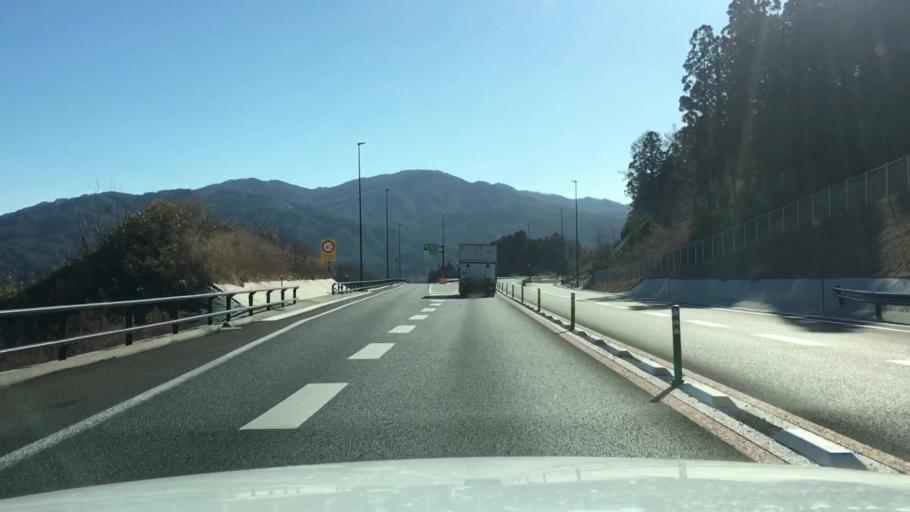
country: JP
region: Iwate
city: Miyako
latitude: 39.5991
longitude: 141.9365
